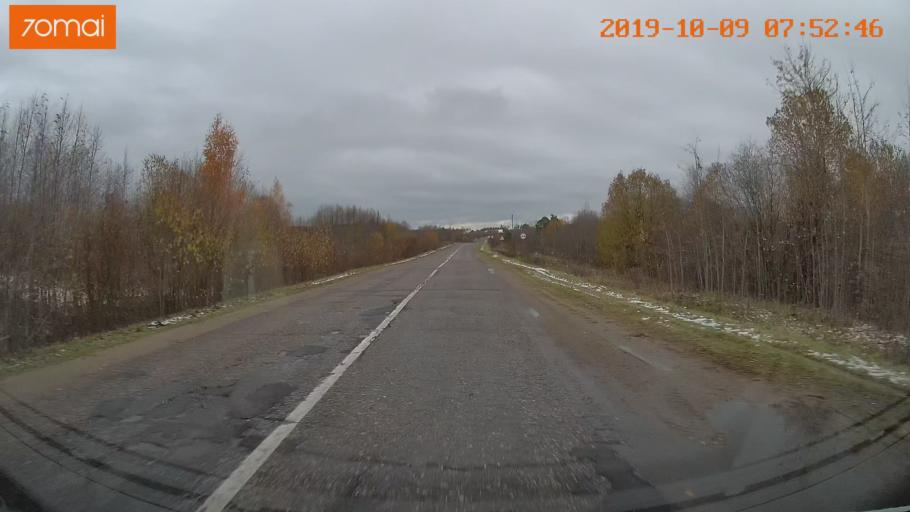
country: RU
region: Jaroslavl
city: Kukoboy
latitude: 58.6935
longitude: 39.8898
